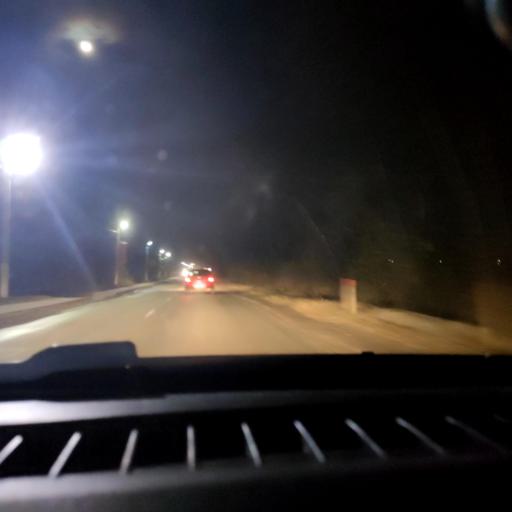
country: RU
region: Voronezj
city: Novaya Usman'
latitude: 51.6429
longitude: 39.3312
